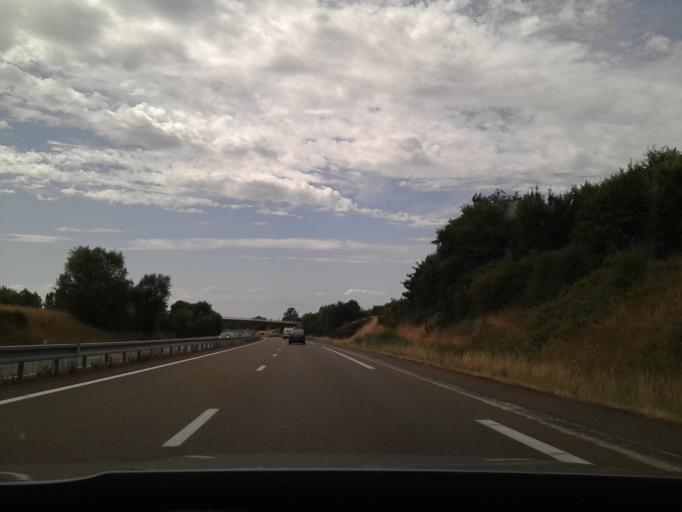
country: FR
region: Pays de la Loire
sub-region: Departement de la Sarthe
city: Sainte-Jamme-sur-Sarthe
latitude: 48.1272
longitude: 0.1441
